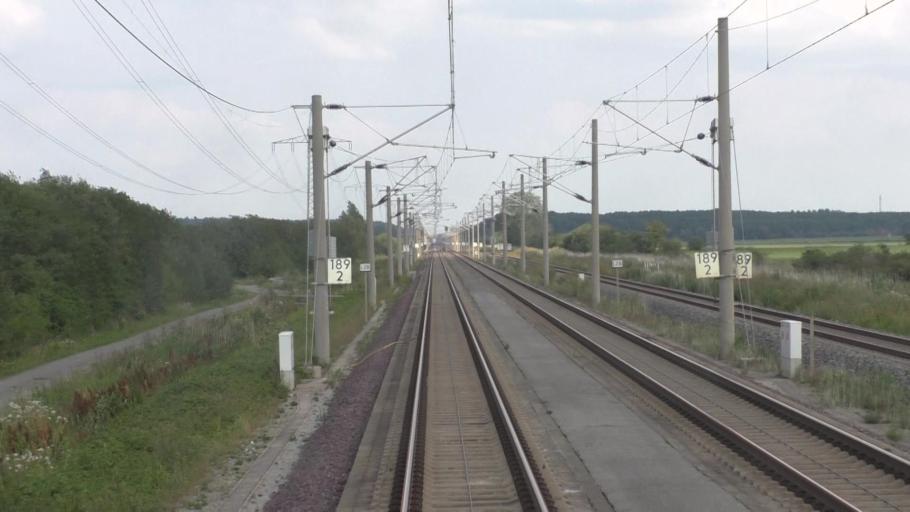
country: DE
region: Saxony-Anhalt
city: Schonhausen
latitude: 52.5905
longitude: 12.0849
